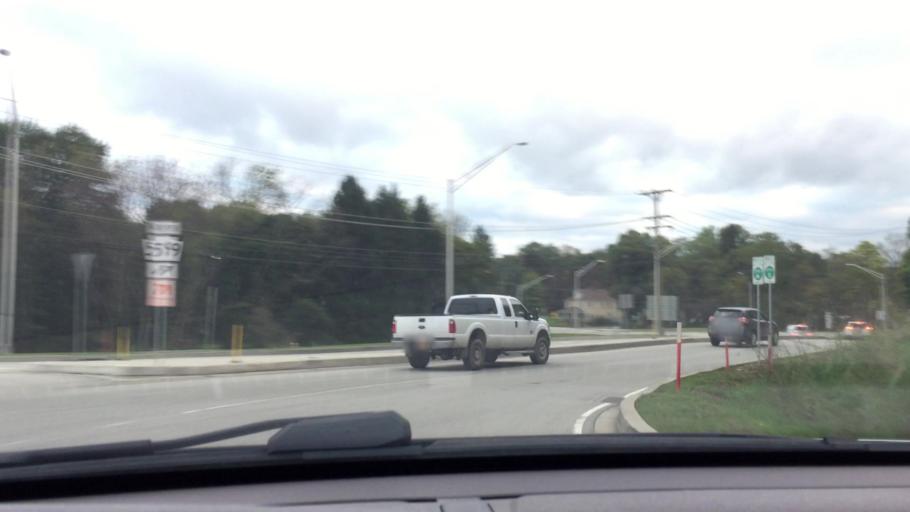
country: US
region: Pennsylvania
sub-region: Washington County
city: Canonsburg
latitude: 40.2038
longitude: -80.1262
